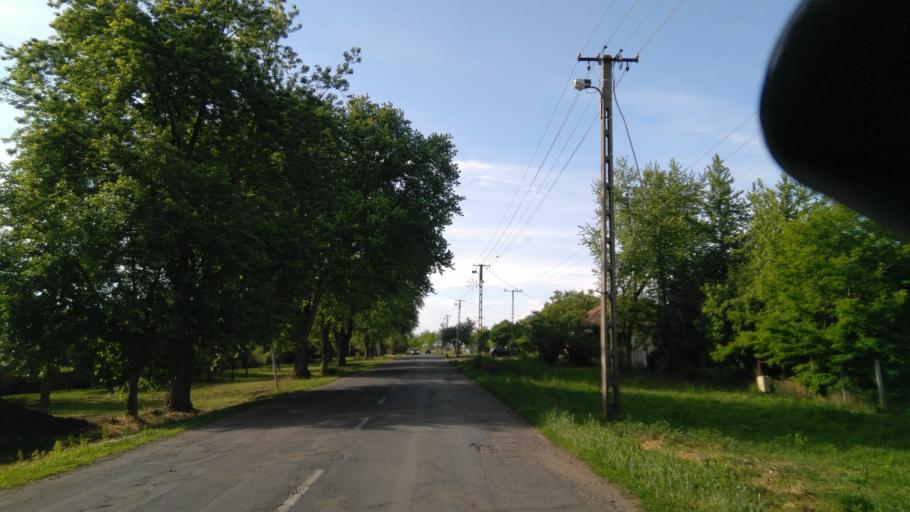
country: HU
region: Bekes
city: Lokoshaza
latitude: 46.4339
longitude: 21.2283
